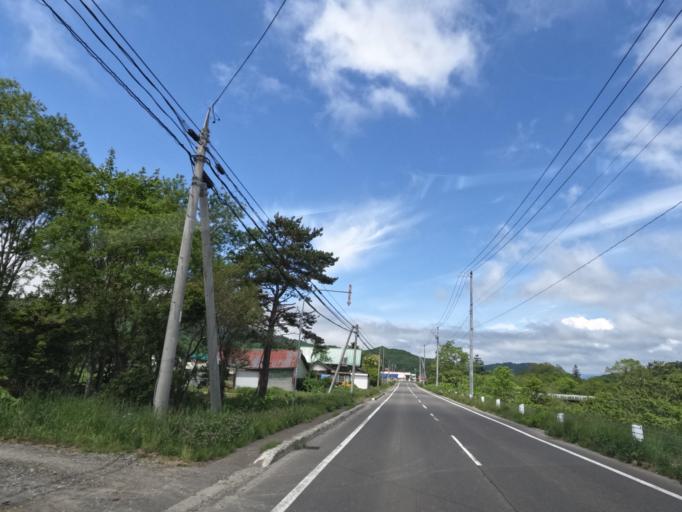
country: JP
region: Hokkaido
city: Tobetsu
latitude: 43.2817
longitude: 141.5361
